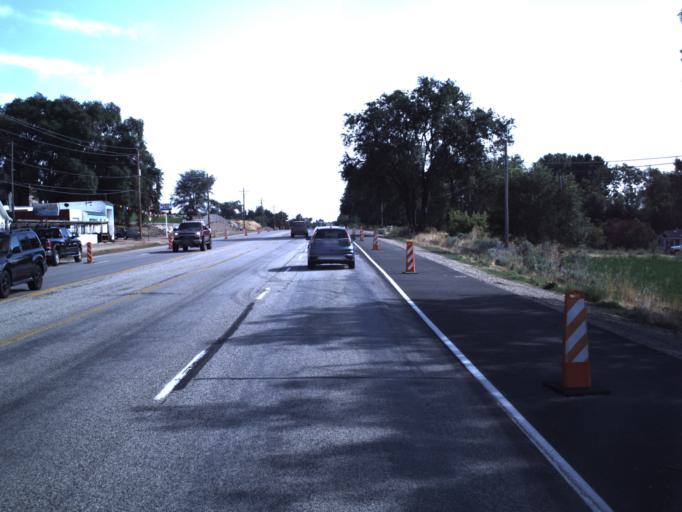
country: US
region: Utah
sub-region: Box Elder County
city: South Willard
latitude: 41.3818
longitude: -112.0323
